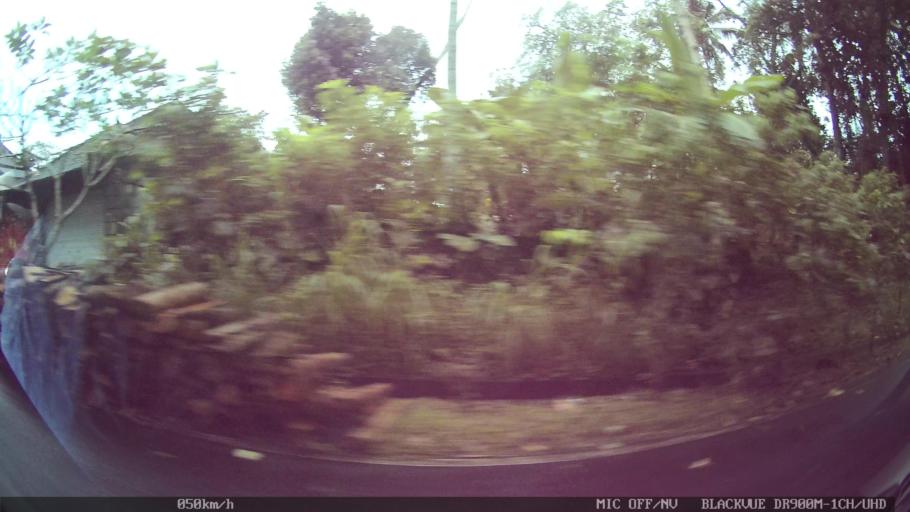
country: ID
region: Bali
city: Pegongan
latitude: -8.4905
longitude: 115.2379
